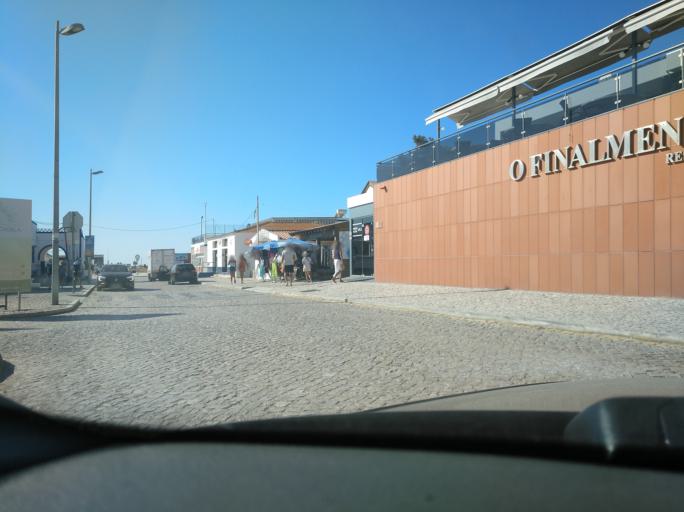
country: PT
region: Faro
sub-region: Vila Real de Santo Antonio
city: Monte Gordo
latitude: 37.1661
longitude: -7.5206
